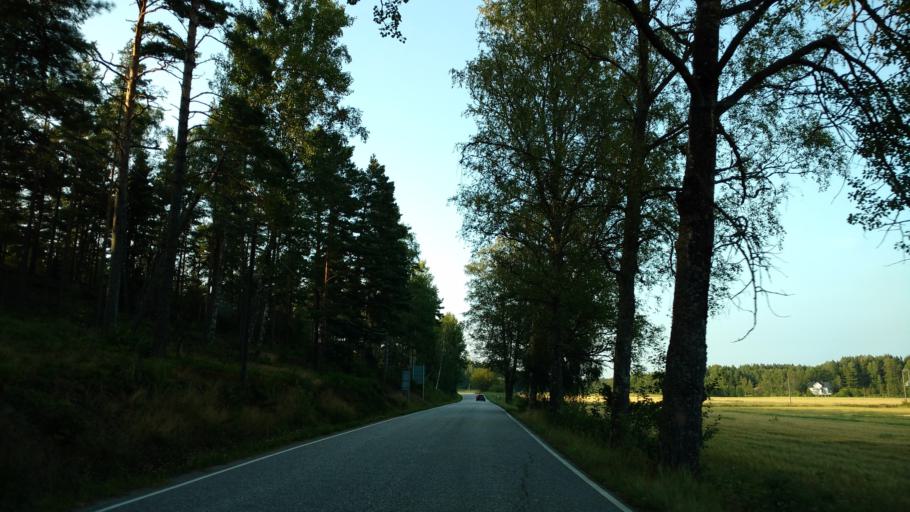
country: FI
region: Varsinais-Suomi
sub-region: Aboland-Turunmaa
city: Dragsfjaerd
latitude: 60.0379
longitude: 22.4424
